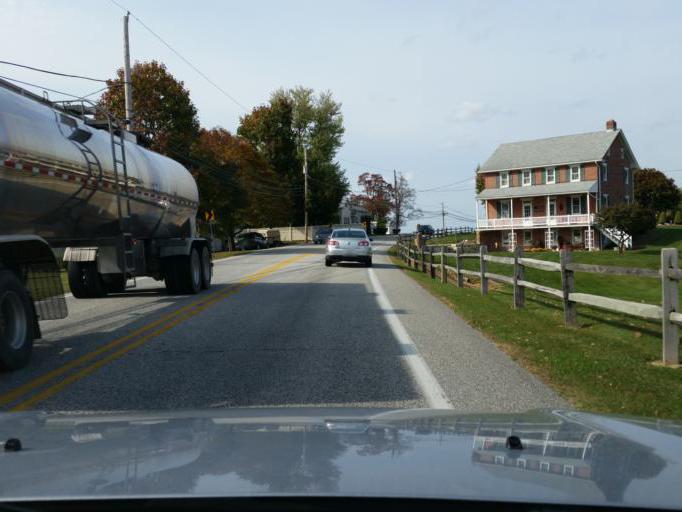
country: US
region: Pennsylvania
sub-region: Dauphin County
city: Skyline View
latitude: 40.3229
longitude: -76.7096
